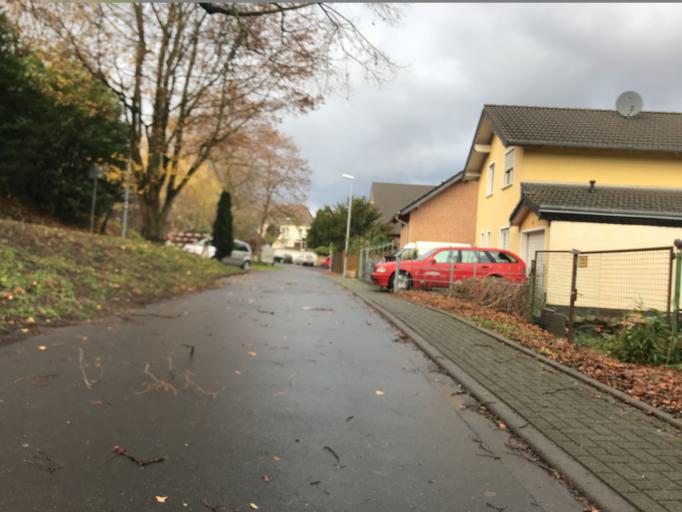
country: DE
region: North Rhine-Westphalia
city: Wesseling
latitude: 50.8281
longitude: 6.9514
